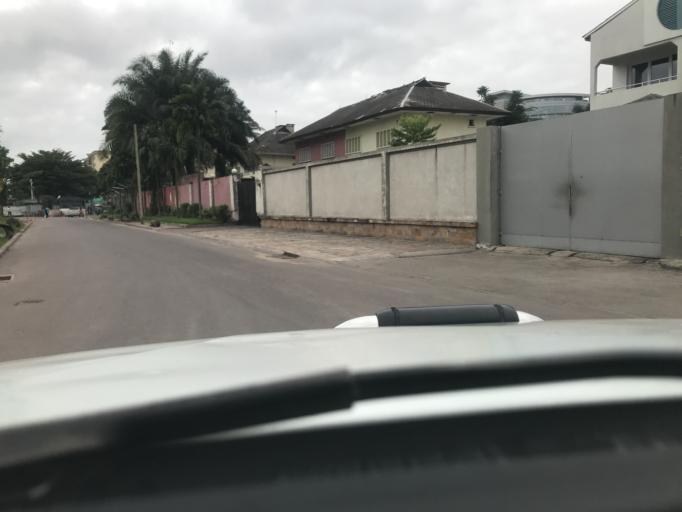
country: CD
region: Kinshasa
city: Kinshasa
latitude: -4.3144
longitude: 15.2855
